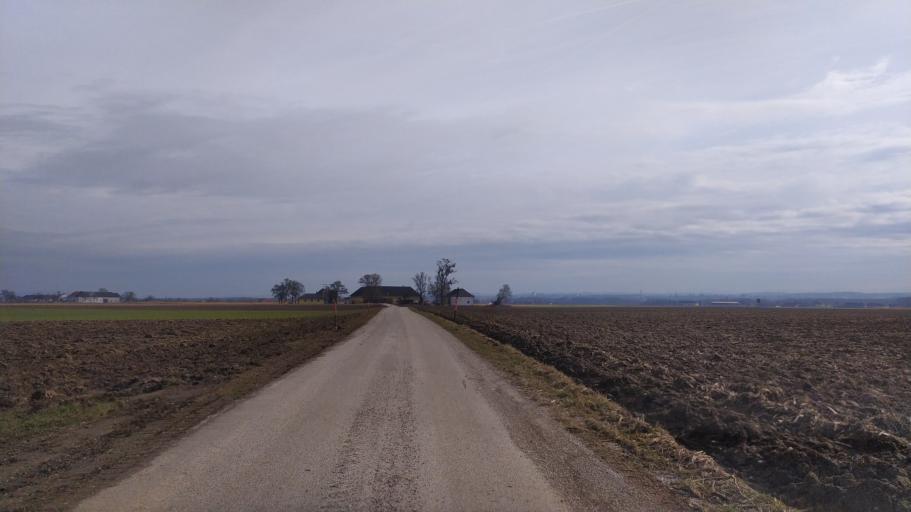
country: AT
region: Upper Austria
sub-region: Politischer Bezirk Perg
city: Perg
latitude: 48.1926
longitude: 14.6608
